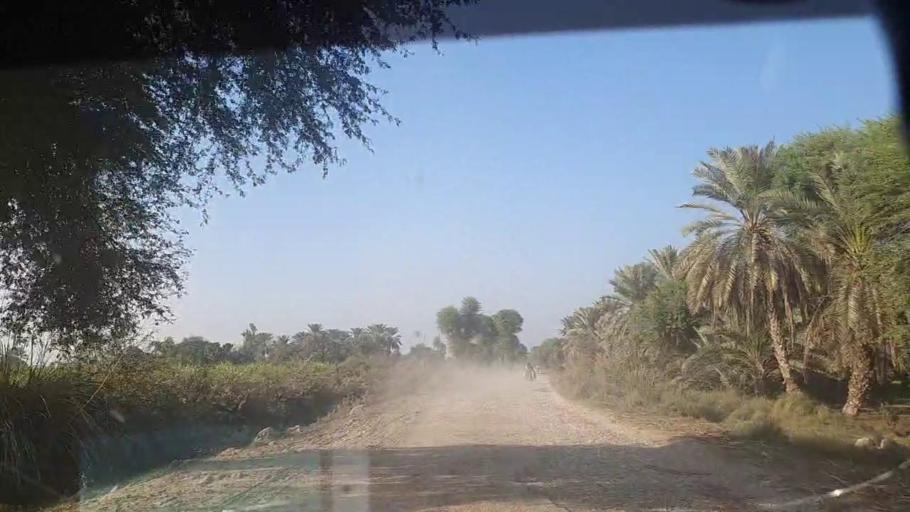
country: PK
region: Sindh
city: Sobhadero
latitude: 27.2668
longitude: 68.3484
